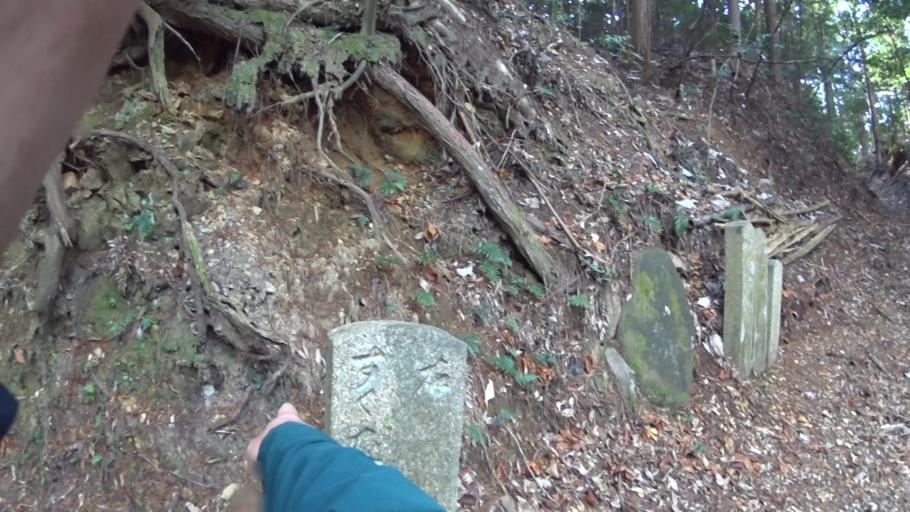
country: JP
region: Kyoto
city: Uji
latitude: 34.9441
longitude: 135.8351
